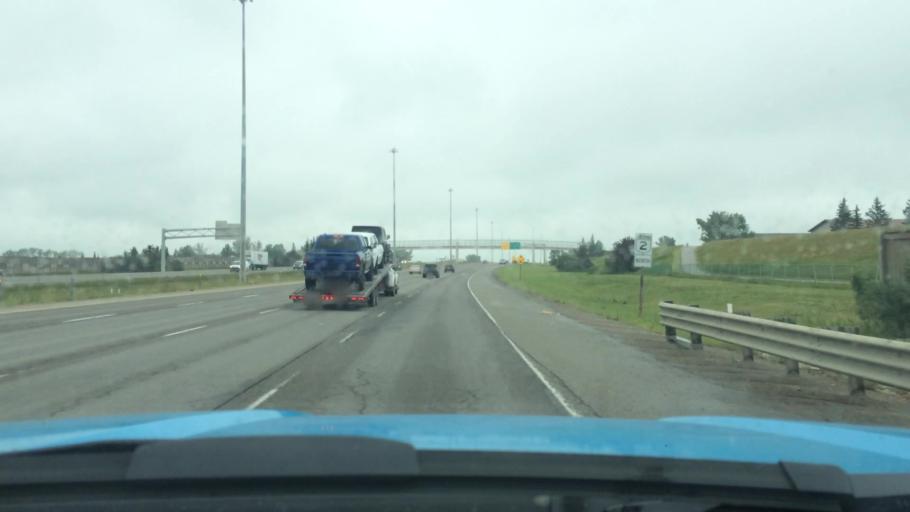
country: CA
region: Alberta
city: Airdrie
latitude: 51.2793
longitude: -114.0015
